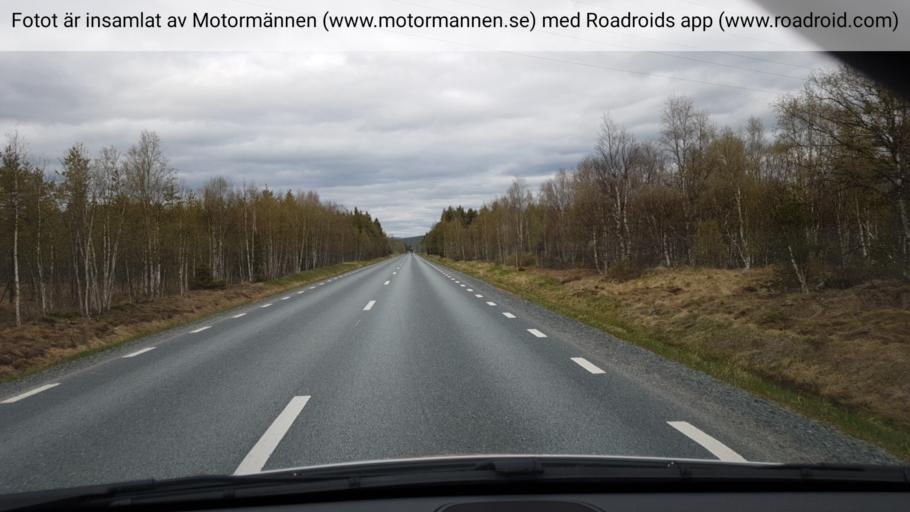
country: SE
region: Vaesterbotten
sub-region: Sorsele Kommun
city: Sorsele
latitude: 65.5163
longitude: 17.5397
